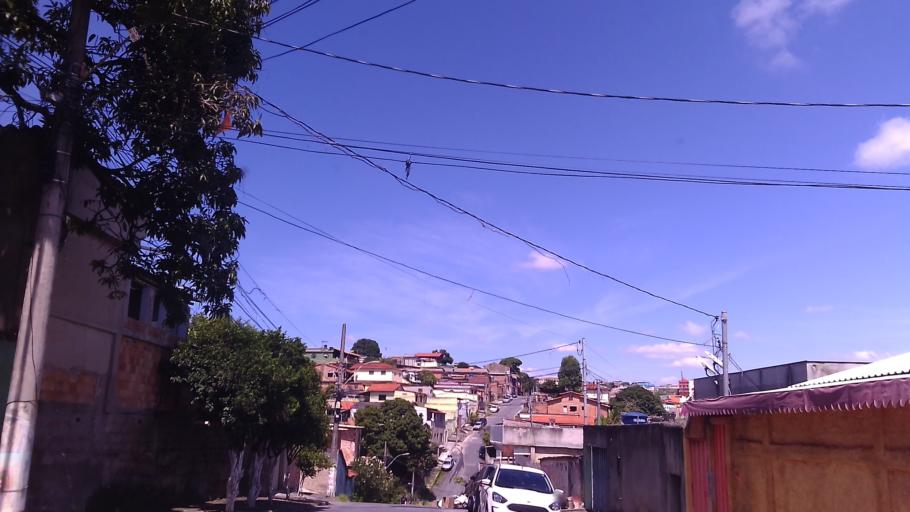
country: BR
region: Minas Gerais
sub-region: Belo Horizonte
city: Belo Horizonte
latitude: -19.8624
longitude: -43.9072
